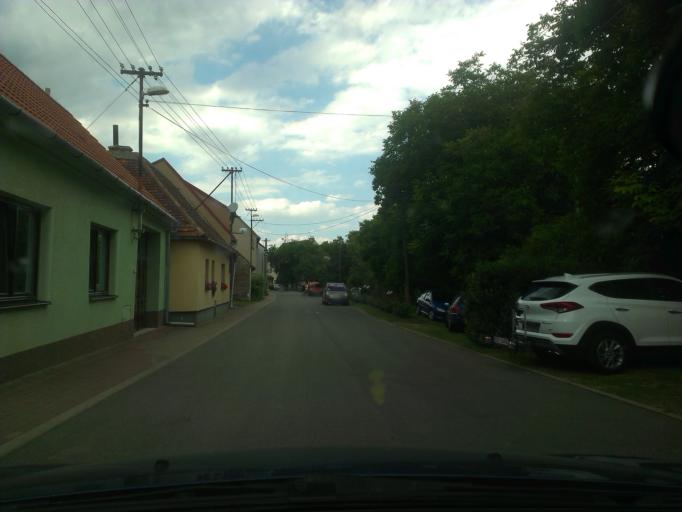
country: CZ
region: South Moravian
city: Velka nad Velickou
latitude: 48.8621
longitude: 17.5327
